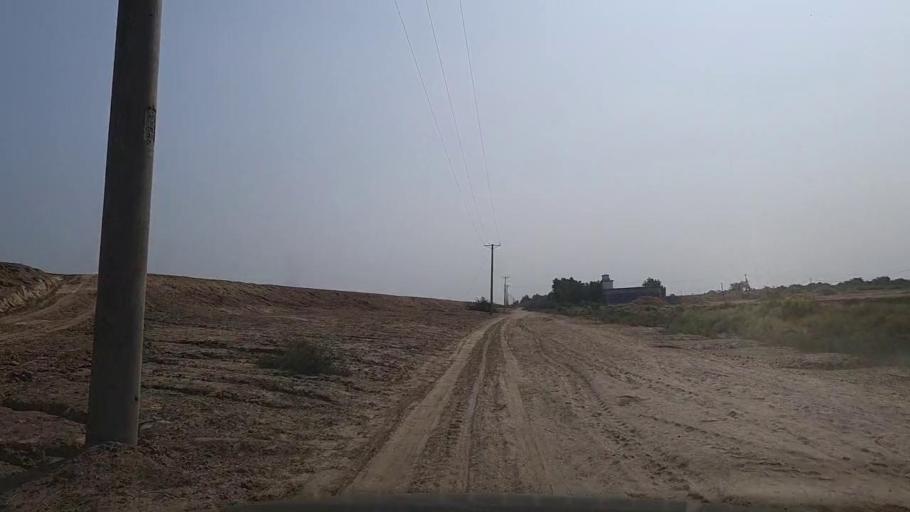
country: PK
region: Sindh
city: Chuhar Jamali
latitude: 24.5591
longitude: 67.9149
